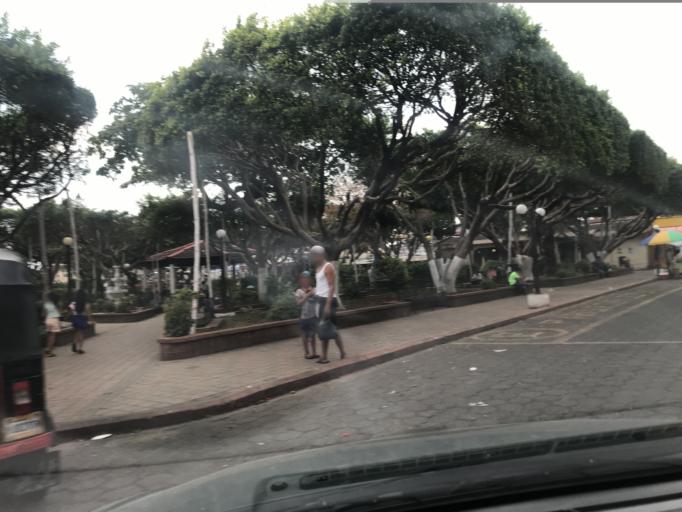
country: GT
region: Suchitepeque
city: San Francisco Zapotitlan
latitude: 14.5898
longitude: -91.5209
